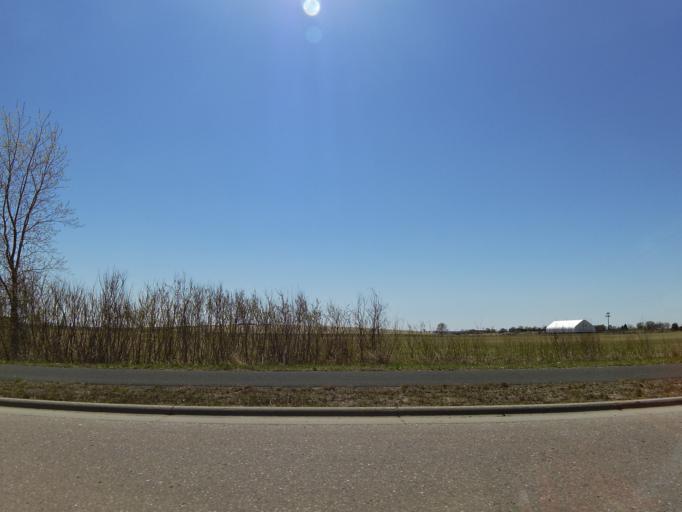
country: US
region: Minnesota
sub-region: Hennepin County
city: Eden Prairie
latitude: 44.8272
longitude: -93.4437
